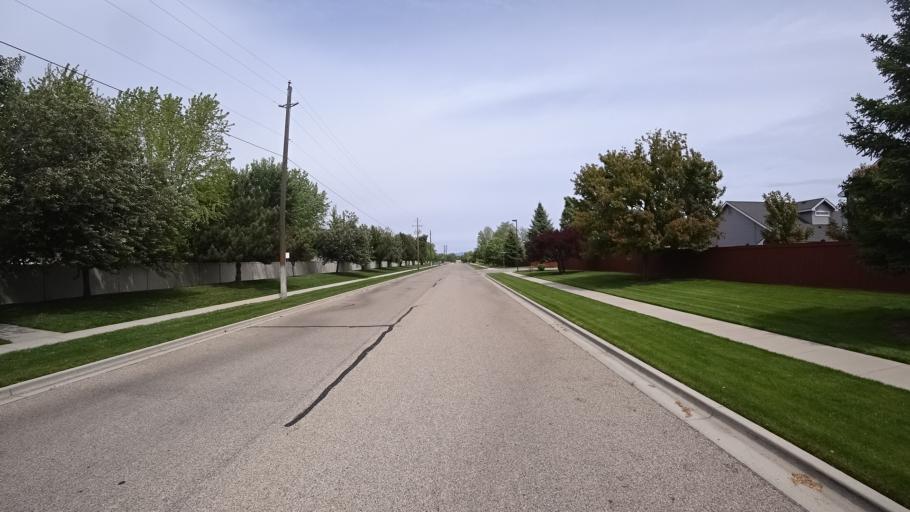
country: US
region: Idaho
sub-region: Ada County
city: Meridian
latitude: 43.5481
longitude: -116.3243
